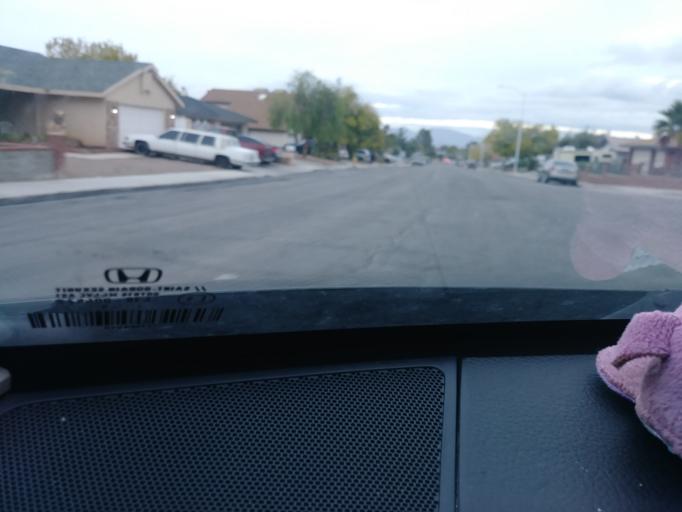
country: US
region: Nevada
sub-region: Clark County
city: Spring Valley
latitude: 36.1770
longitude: -115.2146
